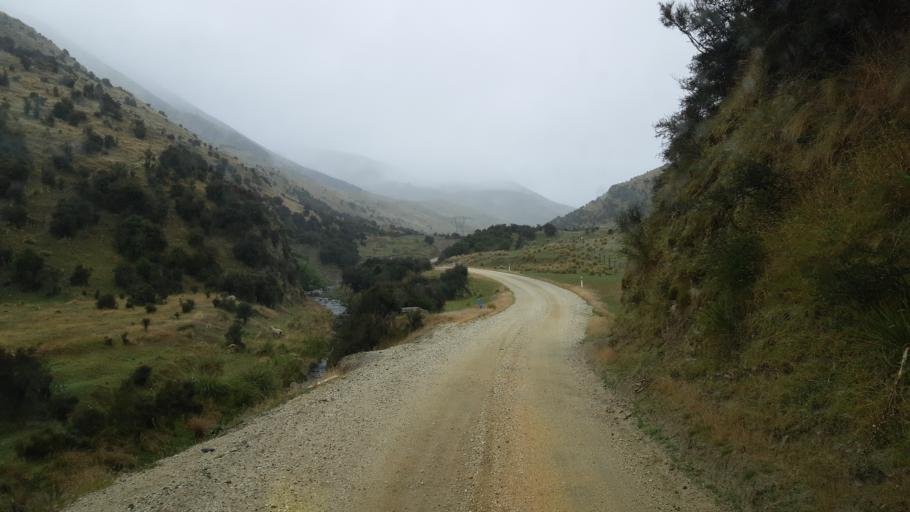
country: NZ
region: Otago
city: Oamaru
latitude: -44.9552
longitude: 170.4467
